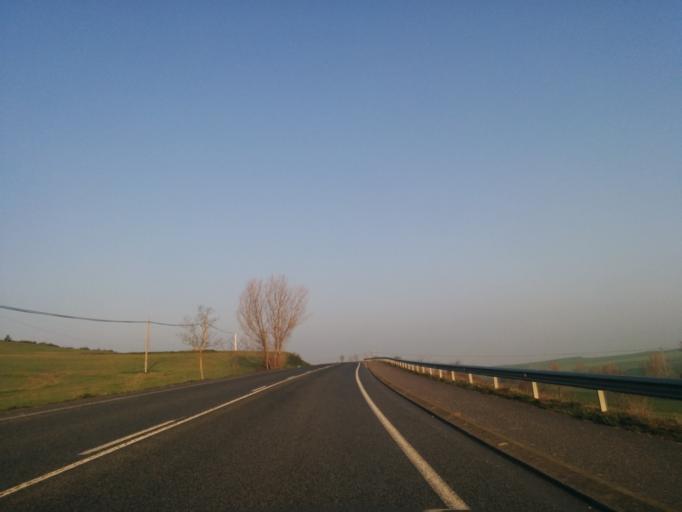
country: ES
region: Navarre
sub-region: Provincia de Navarra
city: Elorz
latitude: 42.7677
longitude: -1.5917
